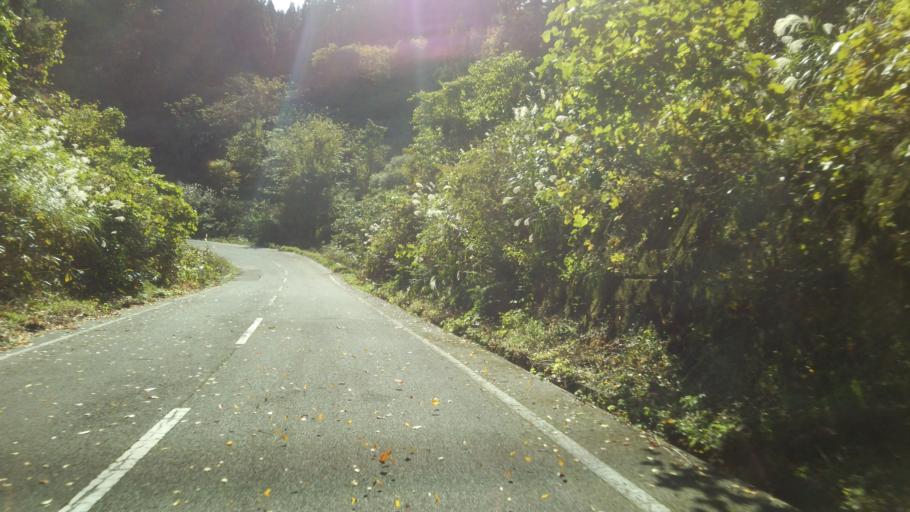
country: JP
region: Fukushima
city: Kitakata
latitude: 37.4342
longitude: 139.7769
